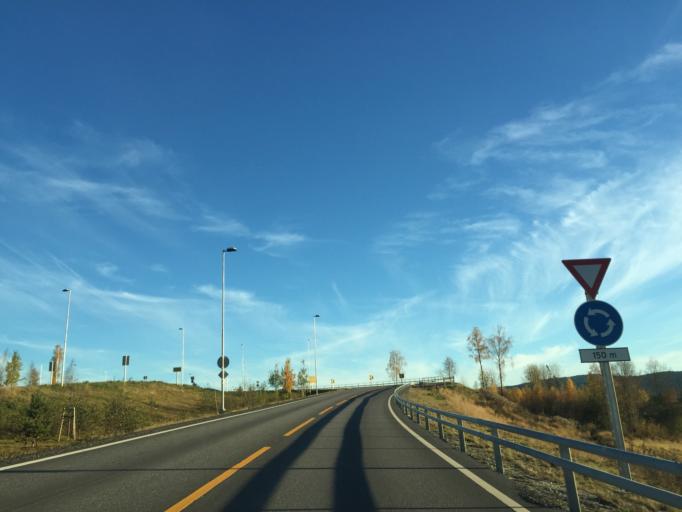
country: NO
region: Hedmark
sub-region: Kongsvinger
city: Spetalen
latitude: 60.2090
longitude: 11.8872
